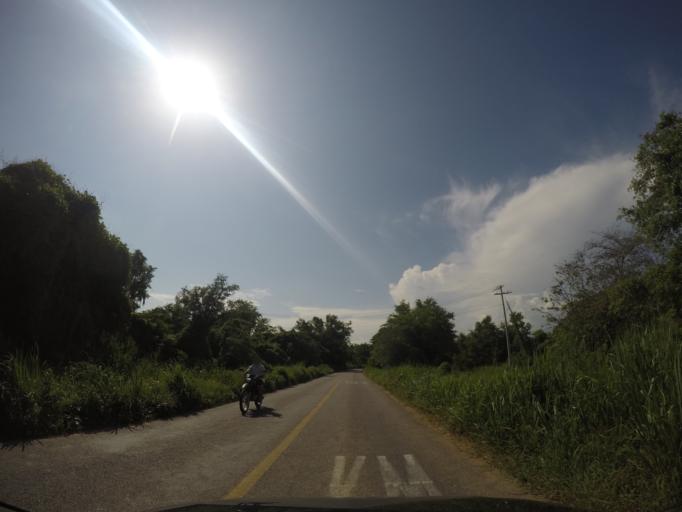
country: MX
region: Oaxaca
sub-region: San Pedro Mixtepec -Dto. 22 -
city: Puerto Escondido
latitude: 15.8906
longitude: -97.1168
